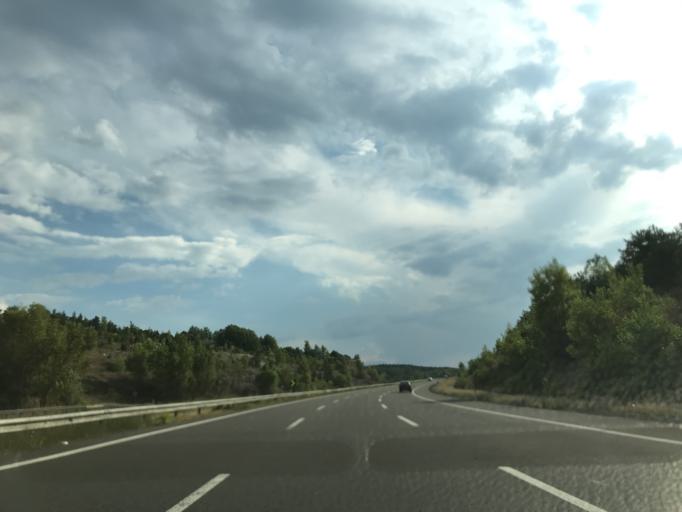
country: TR
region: Bolu
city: Gerede
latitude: 40.6511
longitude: 32.2363
